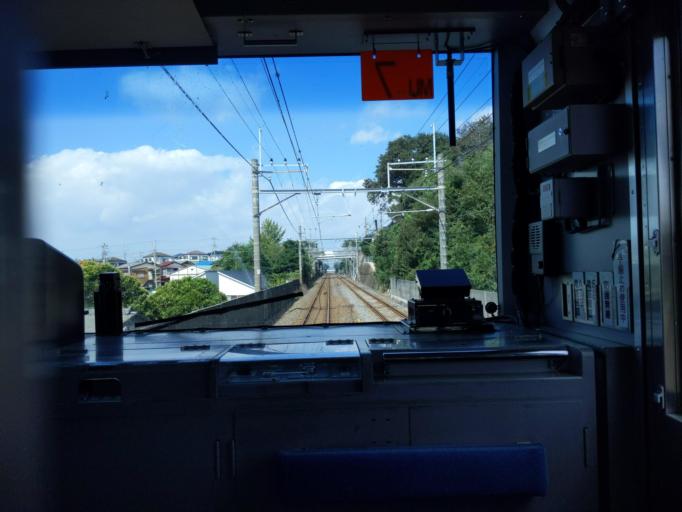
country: JP
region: Chiba
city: Funabashi
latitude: 35.7366
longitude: 139.9632
